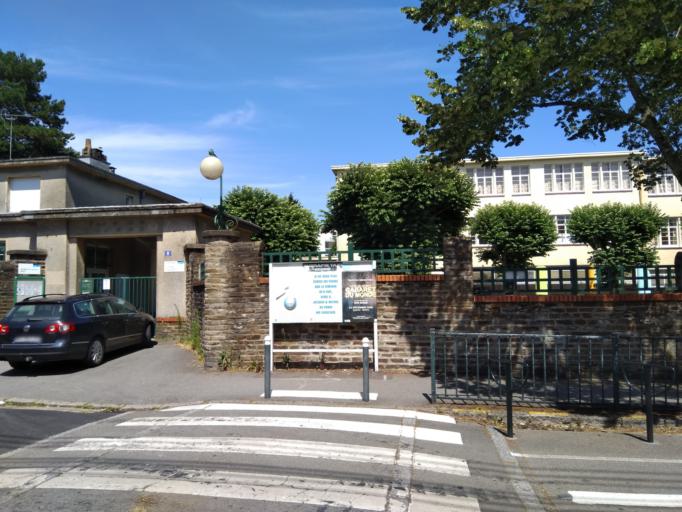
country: FR
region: Pays de la Loire
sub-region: Departement de la Loire-Atlantique
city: Nantes
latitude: 47.2392
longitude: -1.5738
